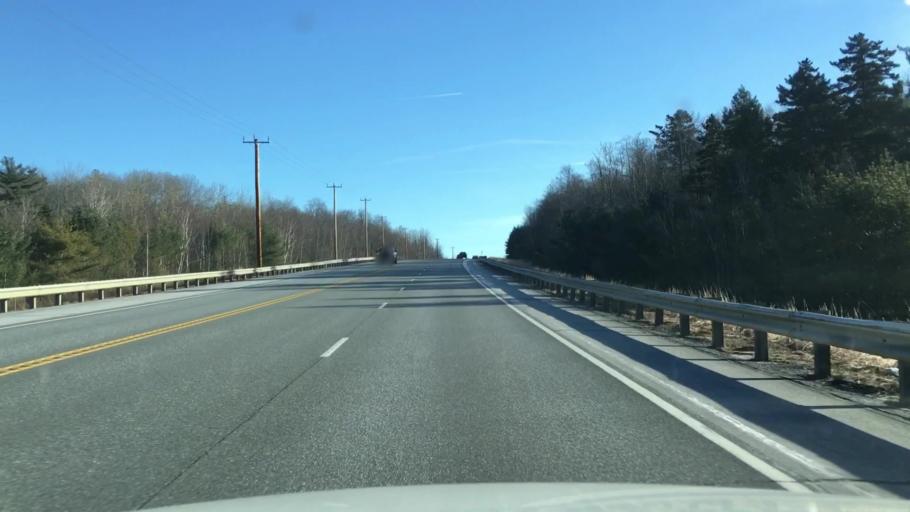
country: US
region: Maine
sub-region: Hancock County
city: Dedham
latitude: 44.6931
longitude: -68.5897
